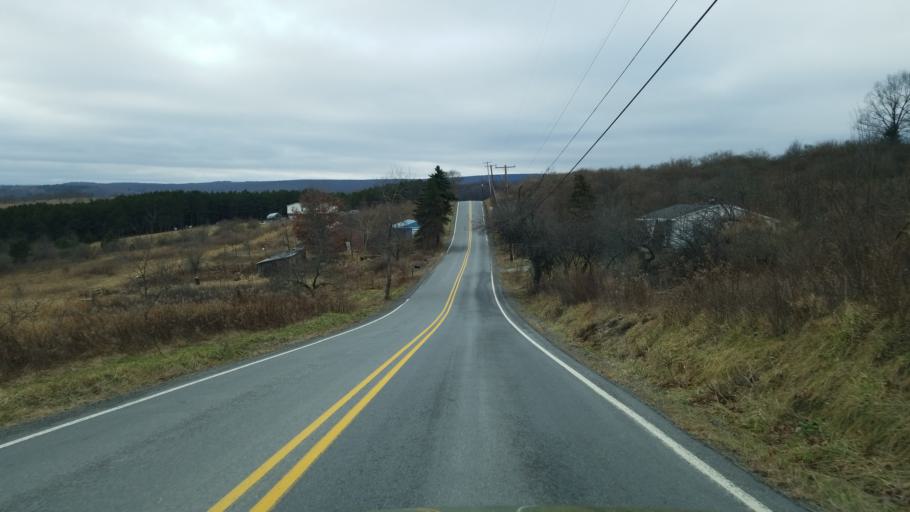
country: US
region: Pennsylvania
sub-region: Clearfield County
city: Hyde
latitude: 41.0355
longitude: -78.4836
